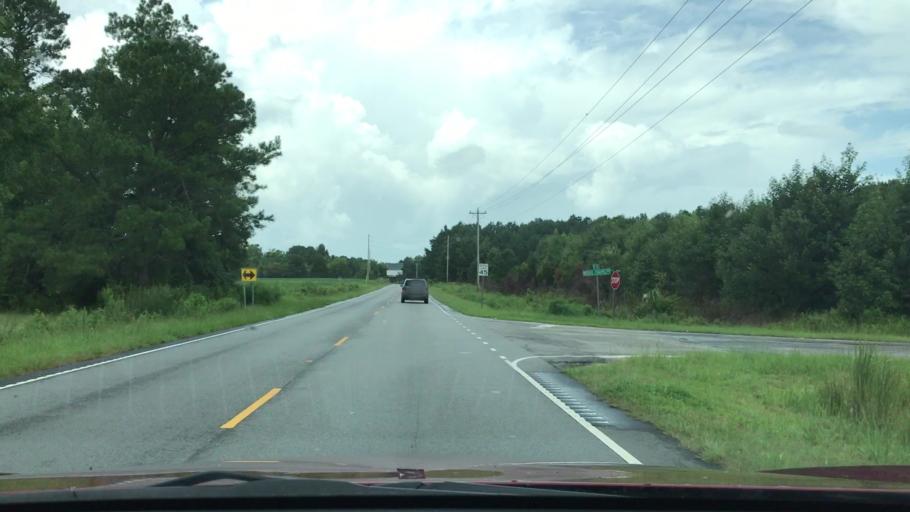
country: US
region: South Carolina
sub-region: Horry County
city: Loris
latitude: 33.9073
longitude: -78.8293
